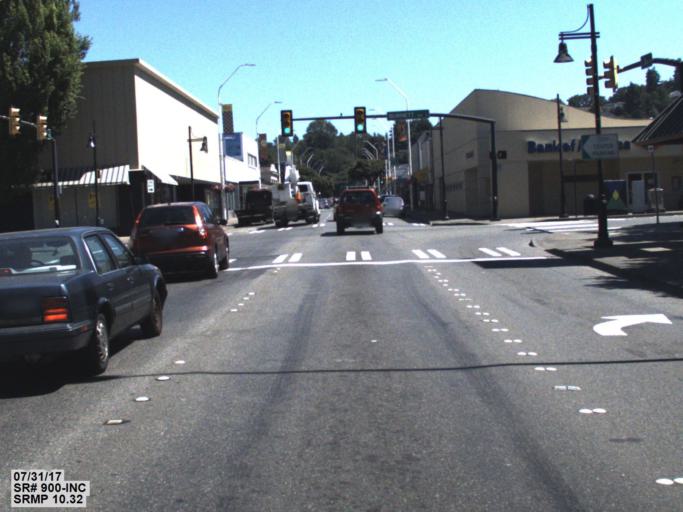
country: US
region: Washington
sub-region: King County
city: Renton
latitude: 47.4797
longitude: -122.2082
